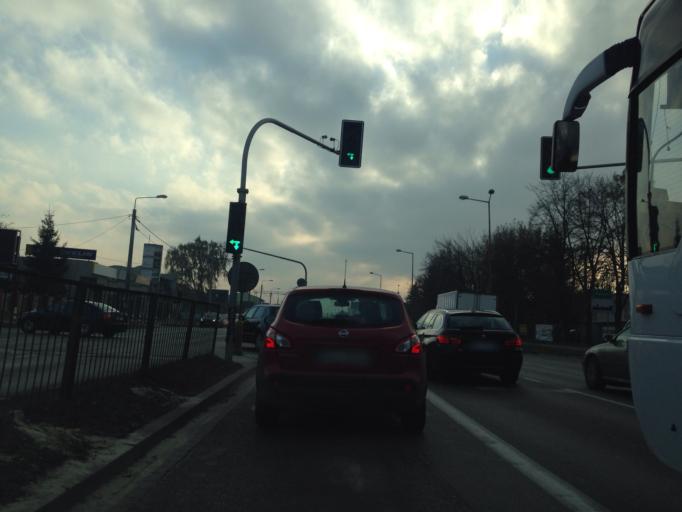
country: PL
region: Masovian Voivodeship
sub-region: Powiat pruszkowski
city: Raszyn
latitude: 52.1636
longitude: 20.9303
